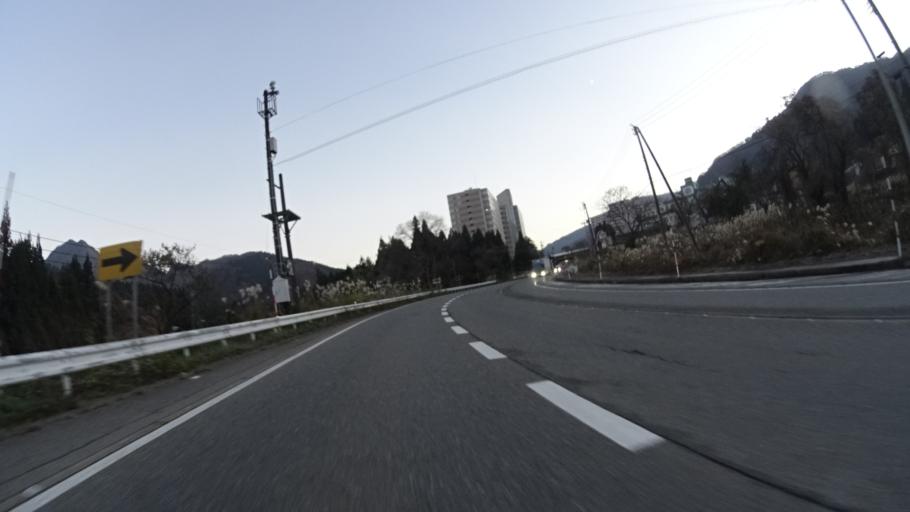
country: JP
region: Niigata
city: Shiozawa
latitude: 36.9709
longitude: 138.8019
